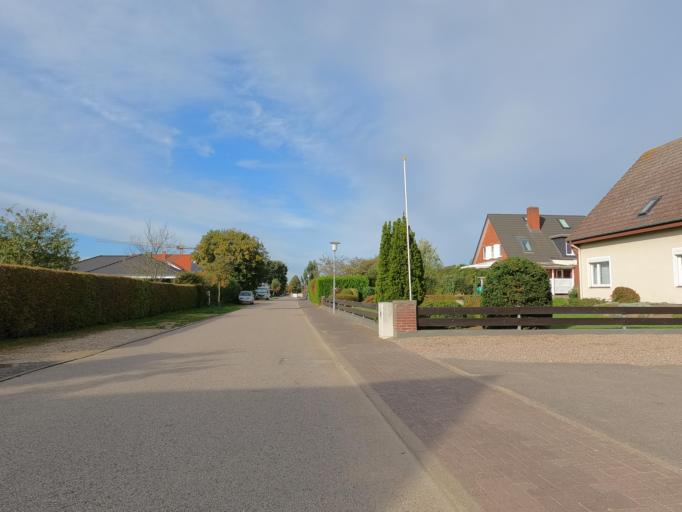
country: DE
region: Schleswig-Holstein
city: Grube
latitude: 54.2262
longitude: 11.0386
